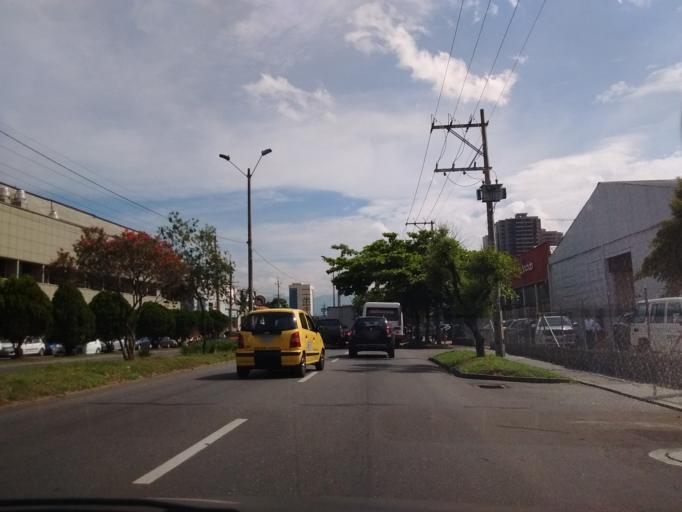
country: CO
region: Antioquia
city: Medellin
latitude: 6.2164
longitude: -75.5759
